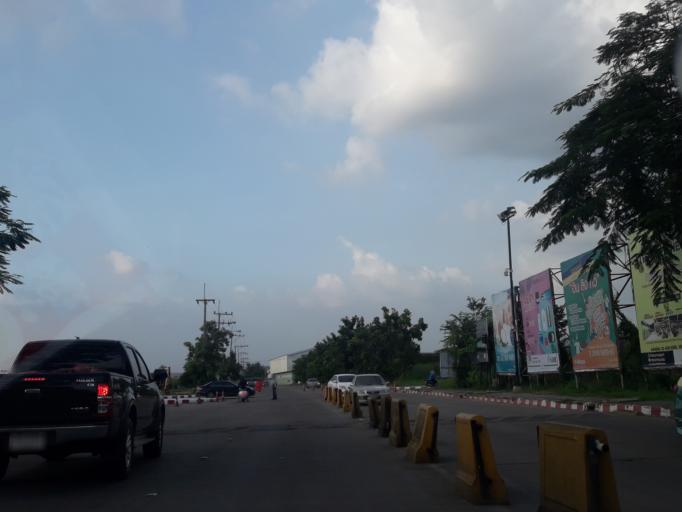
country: TH
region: Phra Nakhon Si Ayutthaya
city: Ban Bang Kadi Pathum Thani
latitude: 13.9944
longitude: 100.6177
